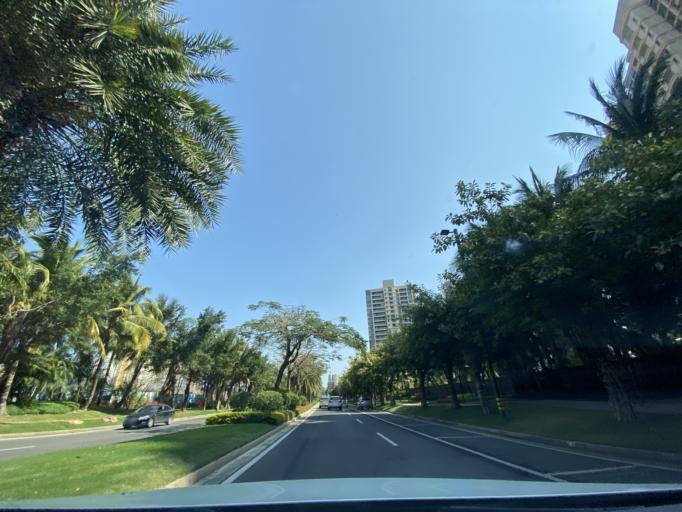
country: CN
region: Hainan
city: Yingzhou
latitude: 18.4060
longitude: 109.8694
